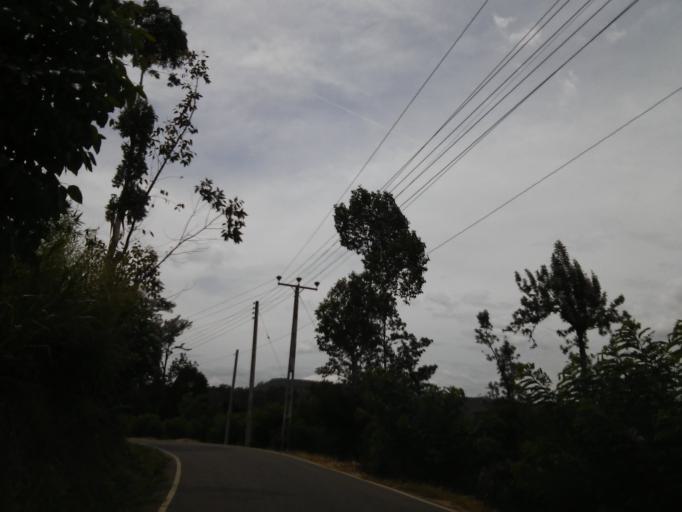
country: LK
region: Uva
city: Haputale
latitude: 6.8478
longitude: 81.0224
